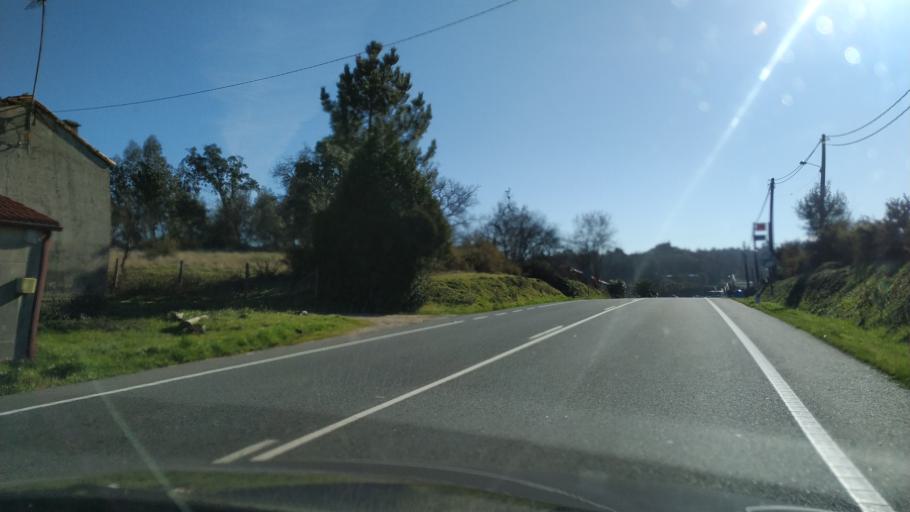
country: ES
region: Galicia
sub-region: Provincia da Coruna
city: Ribeira
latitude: 42.7507
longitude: -8.3499
